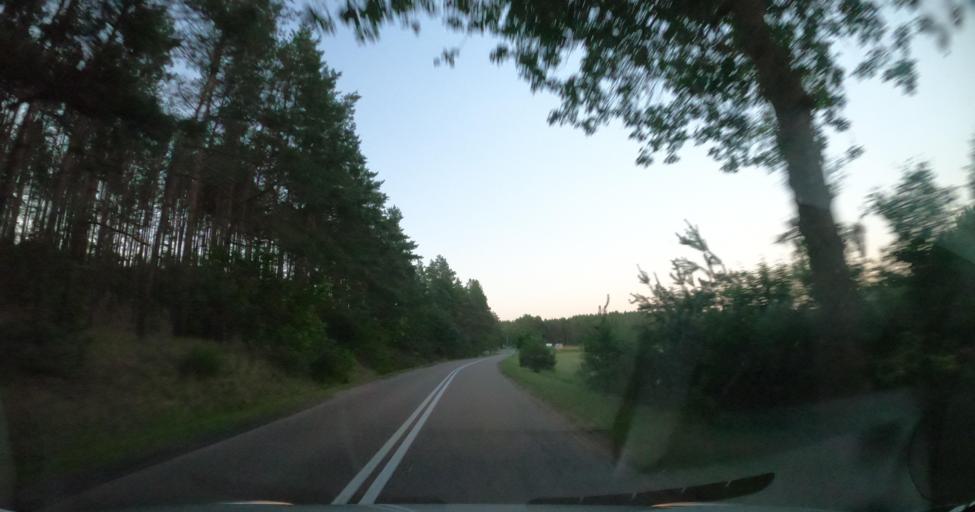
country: PL
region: Pomeranian Voivodeship
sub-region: Powiat wejherowski
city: Luzino
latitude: 54.4757
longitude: 18.0864
